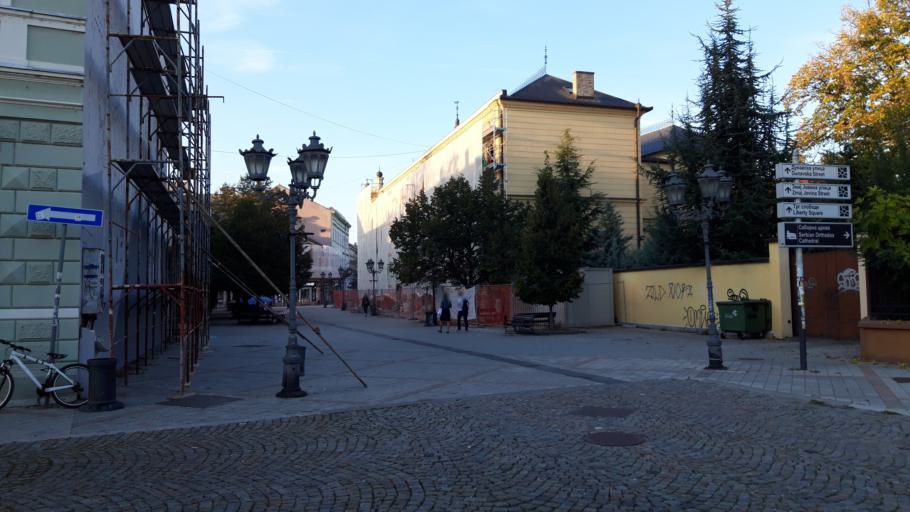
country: RS
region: Autonomna Pokrajina Vojvodina
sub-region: Juznobacki Okrug
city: Novi Sad
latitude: 45.2576
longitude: 19.8487
